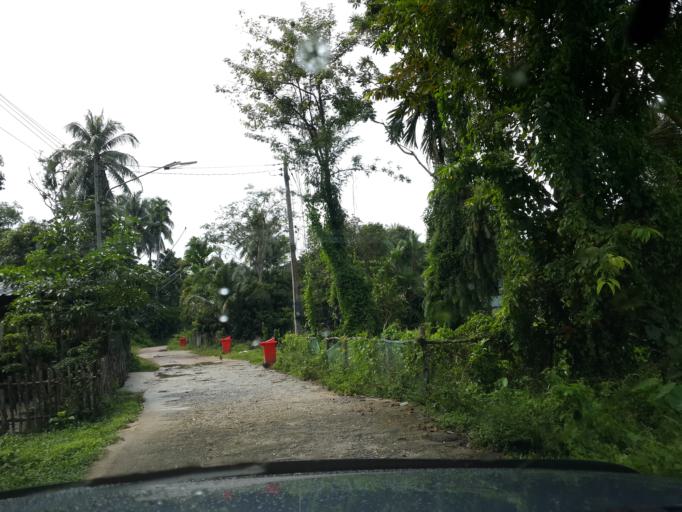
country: TH
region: Narathiwat
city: Rueso
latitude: 6.3833
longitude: 101.5203
